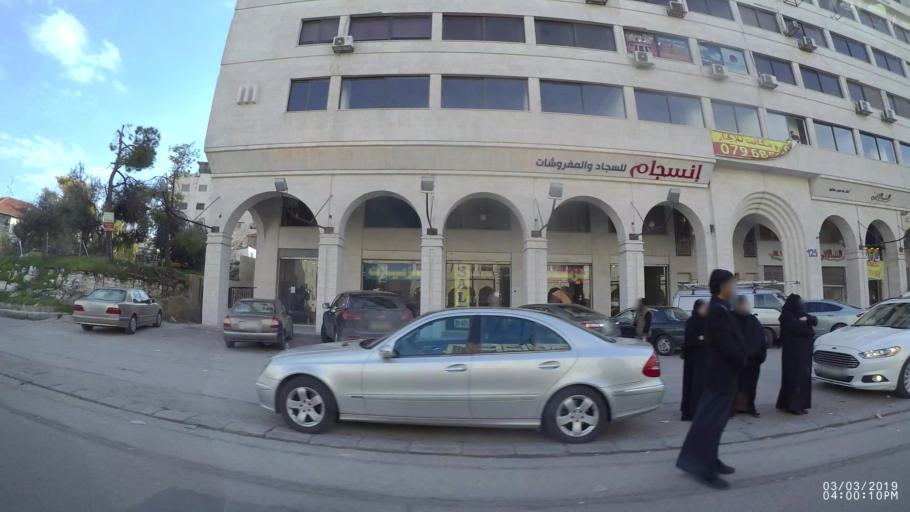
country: JO
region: Amman
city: Al Jubayhah
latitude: 31.9890
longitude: 35.8741
